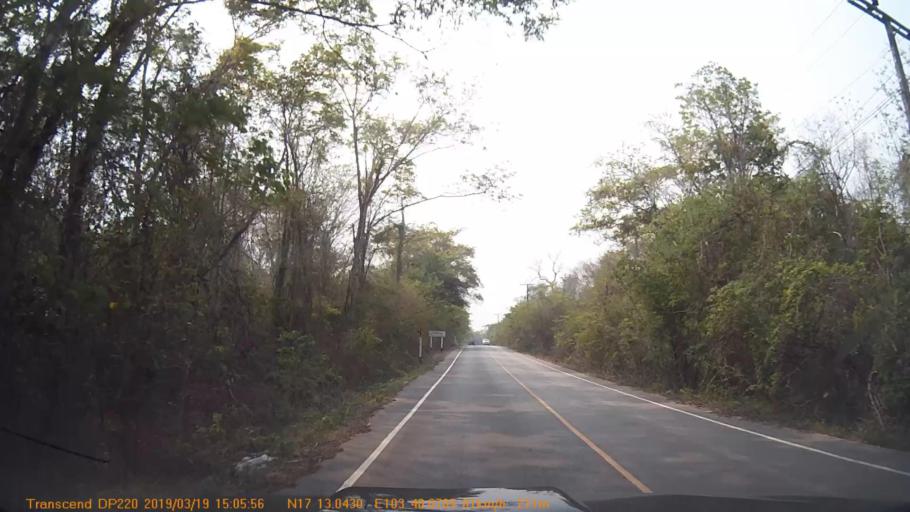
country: TH
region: Sakon Nakhon
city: Nikhom Nam Un
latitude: 17.2175
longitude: 103.8010
